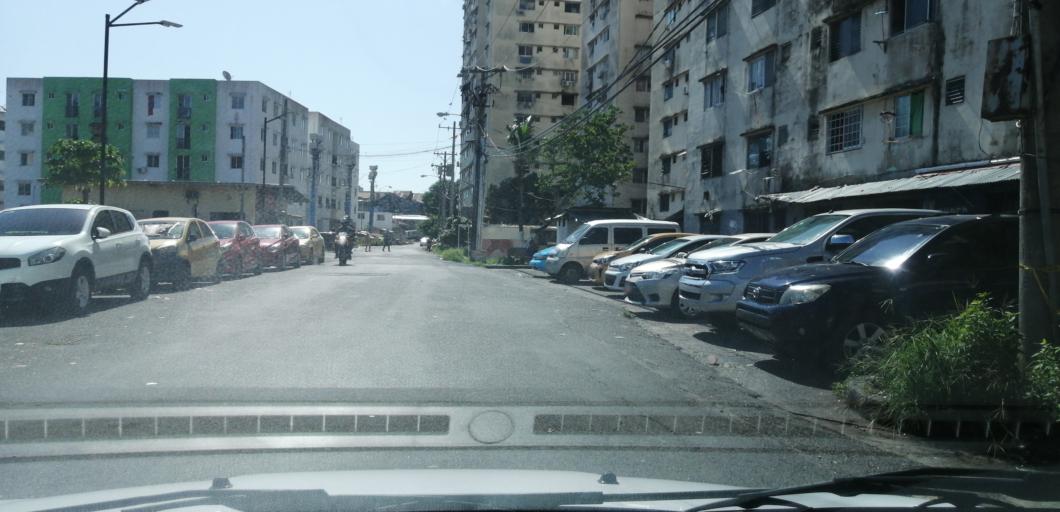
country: PA
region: Panama
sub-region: Distrito de Panama
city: Ancon
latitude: 8.9503
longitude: -79.5409
